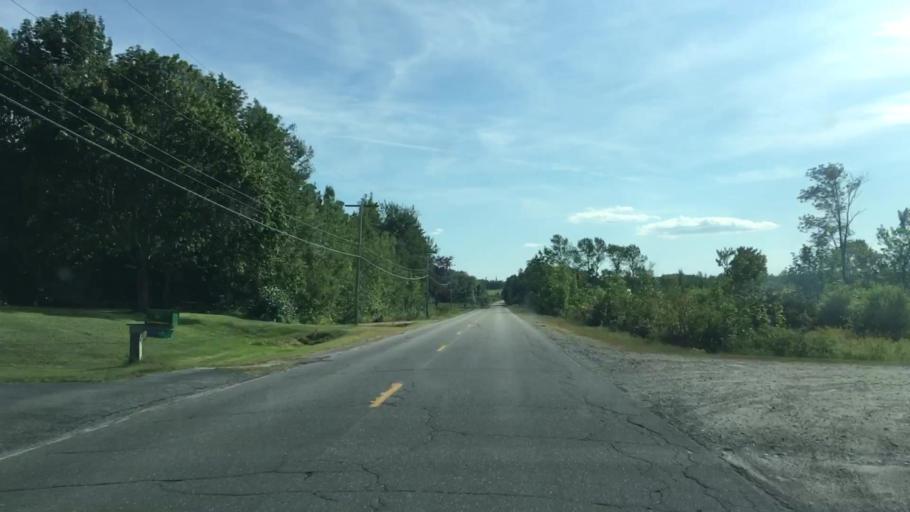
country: US
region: Maine
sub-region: Penobscot County
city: Lincoln
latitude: 45.3278
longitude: -68.5315
